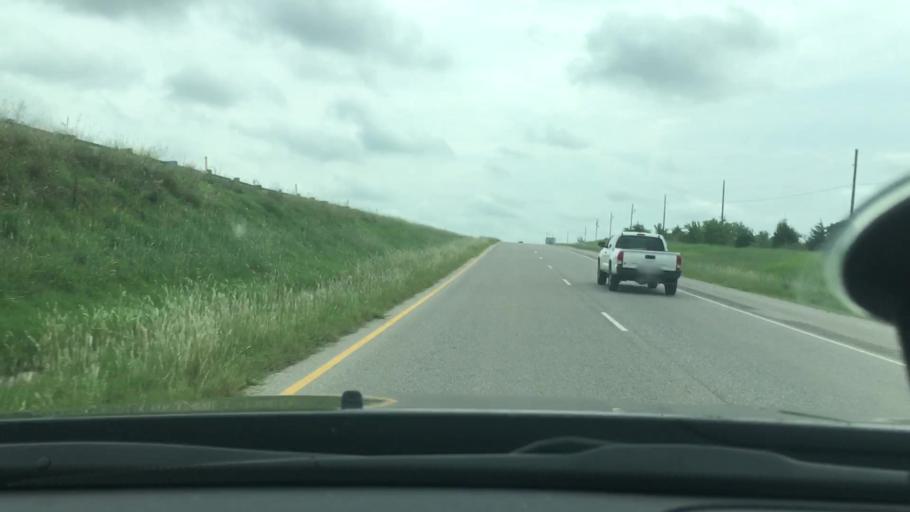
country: US
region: Oklahoma
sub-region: Carter County
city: Wilson
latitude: 34.1728
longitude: -97.4481
